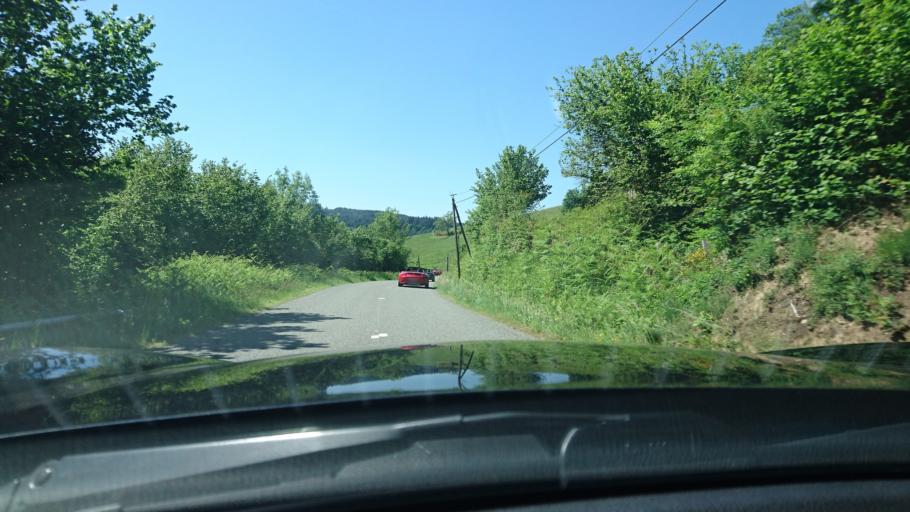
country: FR
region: Rhone-Alpes
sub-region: Departement de la Loire
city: Saint-Just-la-Pendue
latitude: 45.8869
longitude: 4.3023
